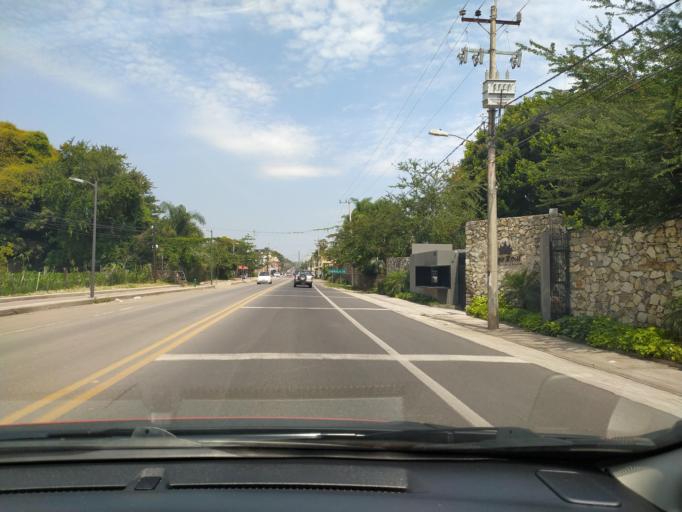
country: MX
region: Jalisco
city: San Juan Cosala
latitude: 20.2895
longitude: -103.3504
